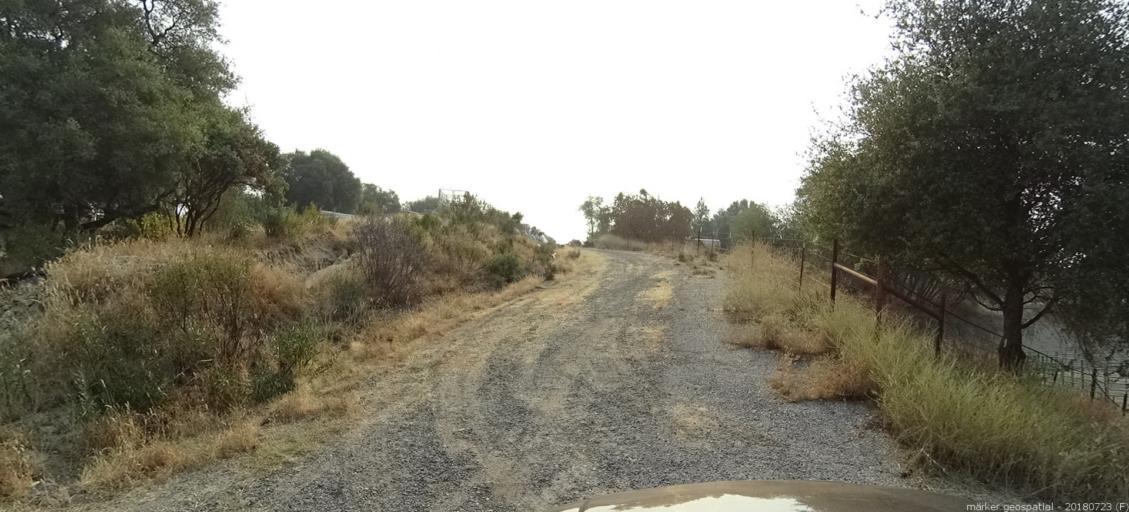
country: US
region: California
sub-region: Madera County
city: Ahwahnee
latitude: 37.3671
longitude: -119.7285
